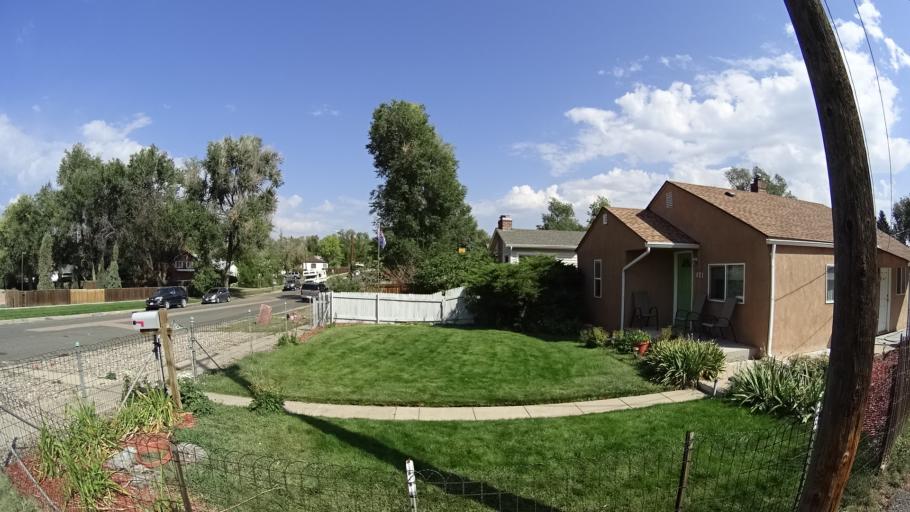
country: US
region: Colorado
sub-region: El Paso County
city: Colorado Springs
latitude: 38.8215
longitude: -104.8026
